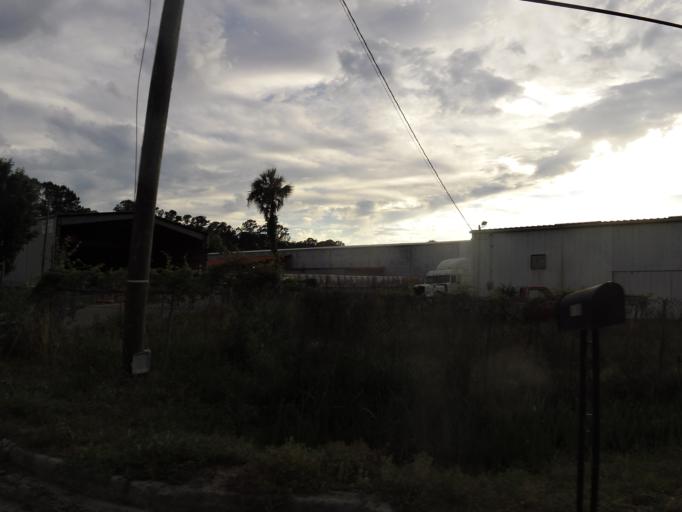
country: US
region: Georgia
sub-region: Chatham County
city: Garden City
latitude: 32.0922
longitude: -81.2004
